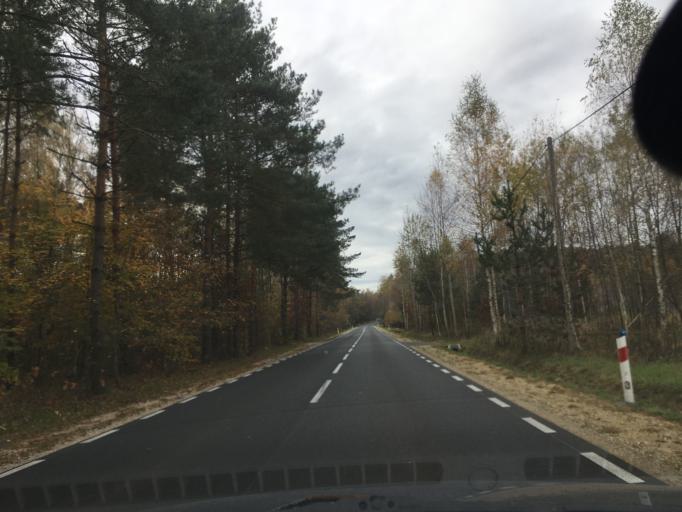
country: PL
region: Lodz Voivodeship
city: Zabia Wola
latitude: 51.9665
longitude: 20.6966
